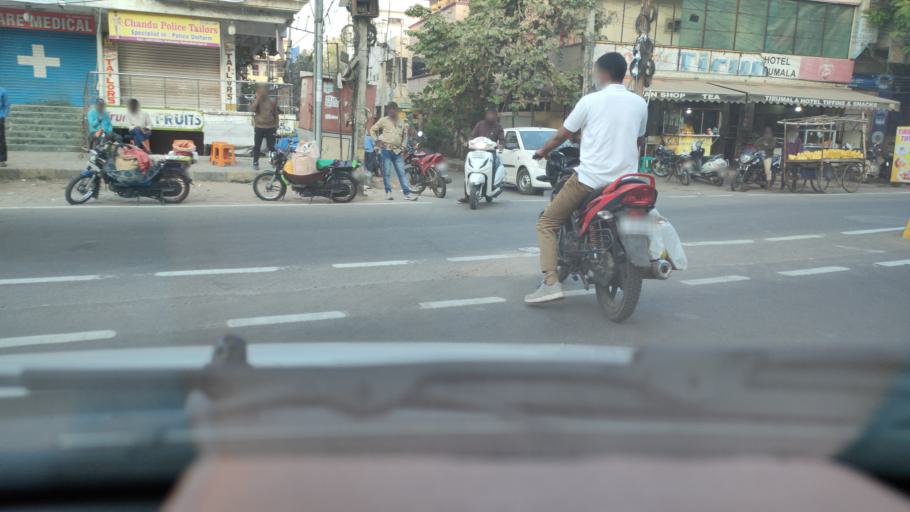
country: IN
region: Telangana
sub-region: Rangareddi
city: Gaddi Annaram
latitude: 17.3867
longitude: 78.5166
